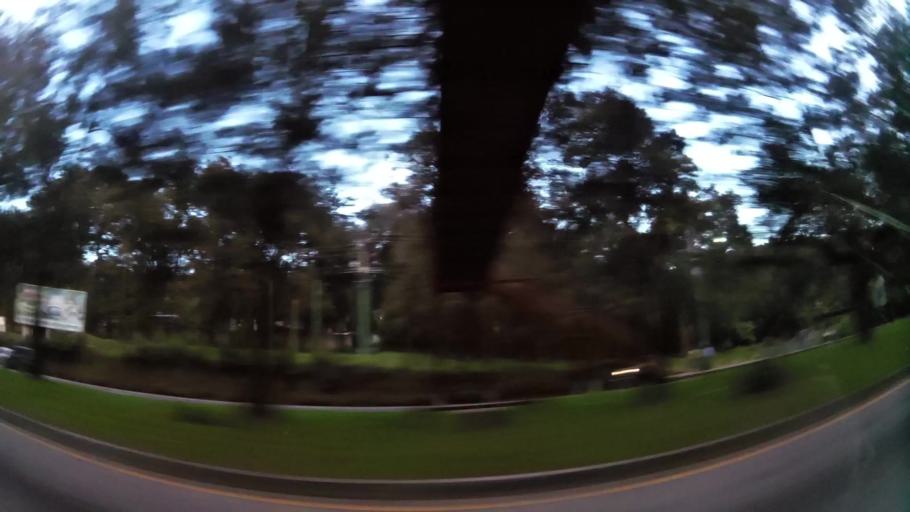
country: GT
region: Sacatepequez
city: San Lucas Sacatepequez
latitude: 14.6010
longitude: -90.6434
